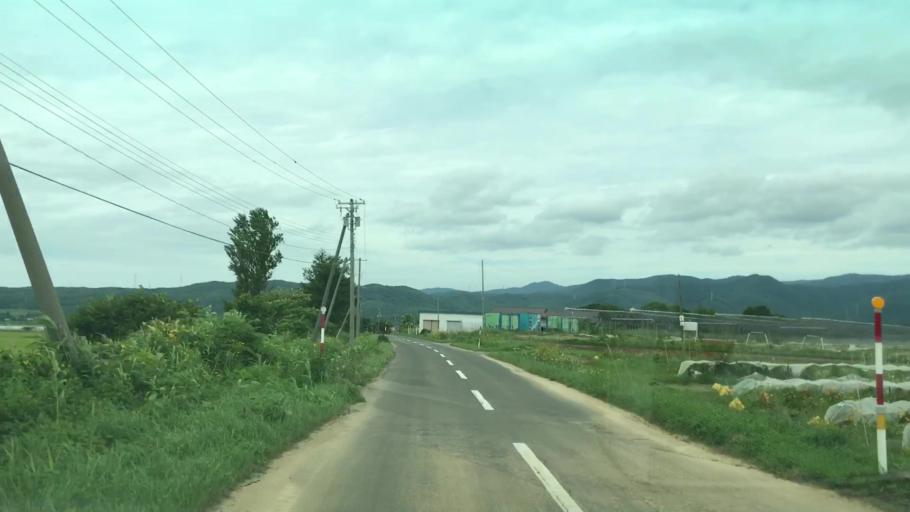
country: JP
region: Hokkaido
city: Iwanai
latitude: 43.0240
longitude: 140.5710
